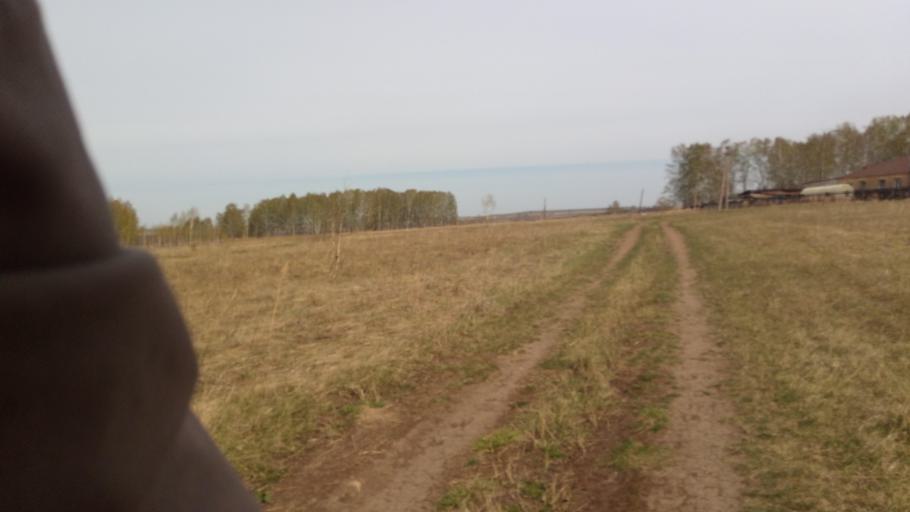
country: RU
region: Chelyabinsk
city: Timiryazevskiy
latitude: 55.0252
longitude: 60.8596
